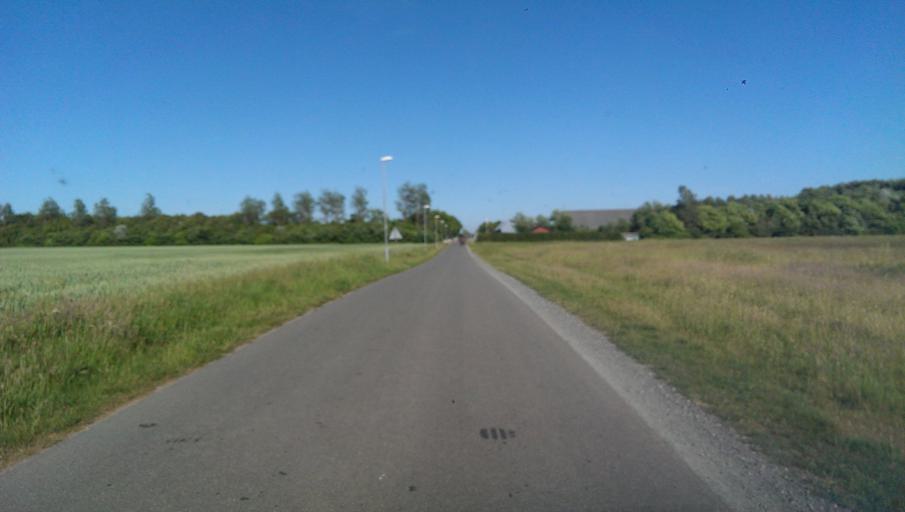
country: DK
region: South Denmark
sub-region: Fano Kommune
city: Nordby
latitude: 55.5213
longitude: 8.3944
